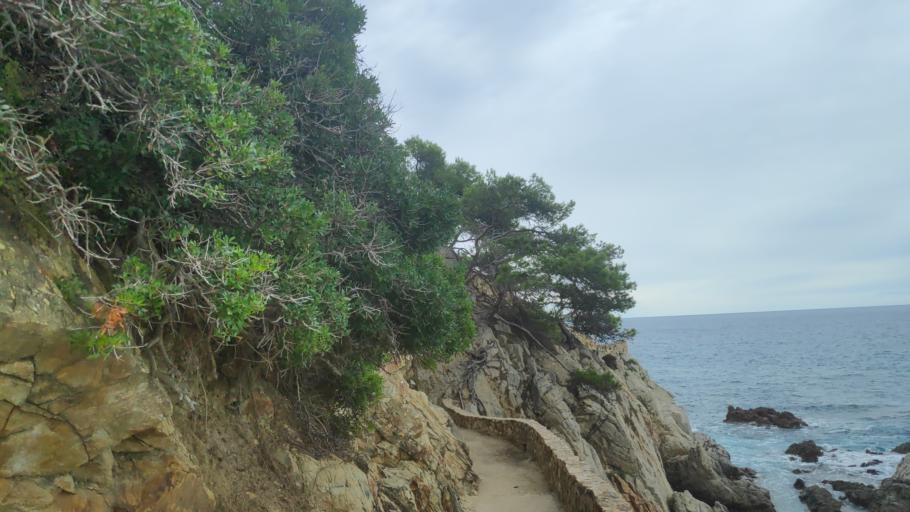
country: ES
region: Catalonia
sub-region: Provincia de Girona
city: Lloret de Mar
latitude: 41.6991
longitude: 2.8596
